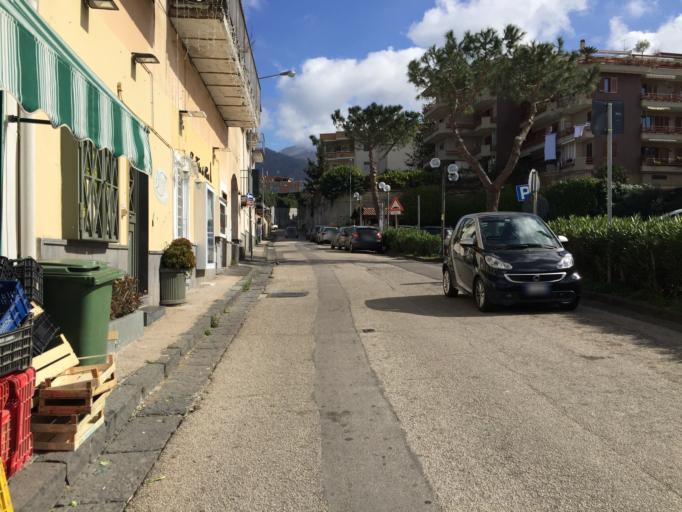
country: IT
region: Campania
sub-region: Provincia di Napoli
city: Massa di Somma
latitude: 40.8429
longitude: 14.3701
